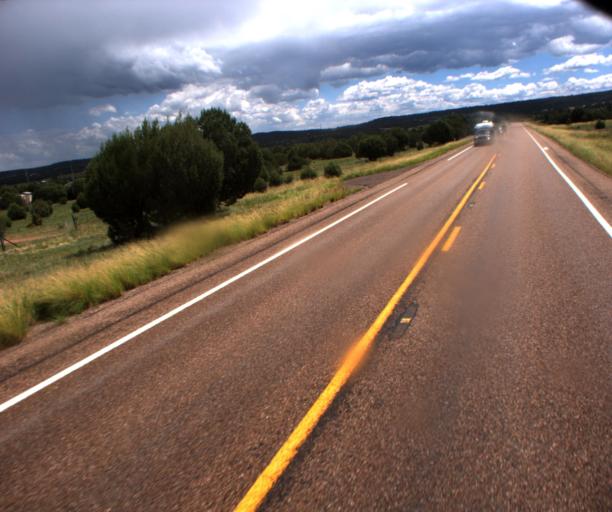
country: US
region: Arizona
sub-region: Navajo County
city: Linden
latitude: 34.3560
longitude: -110.3175
